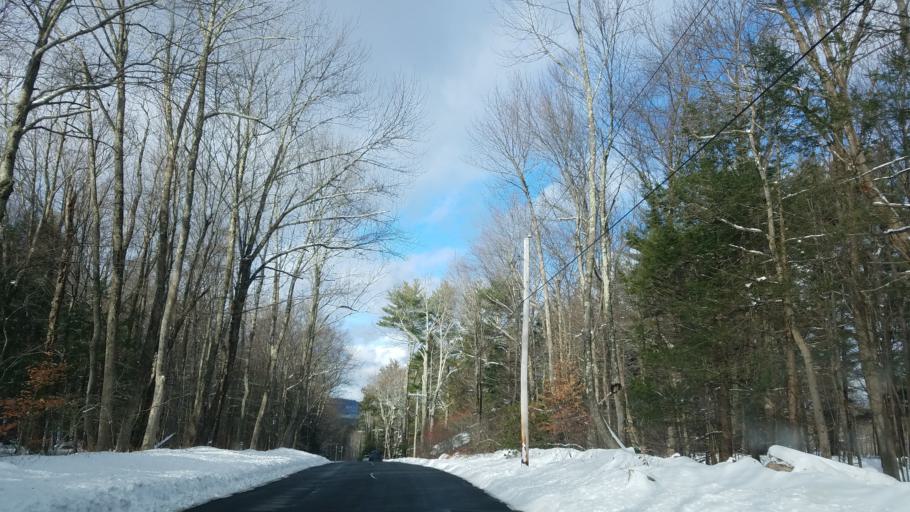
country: US
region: Connecticut
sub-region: Litchfield County
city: Winsted
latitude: 41.9853
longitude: -73.0891
